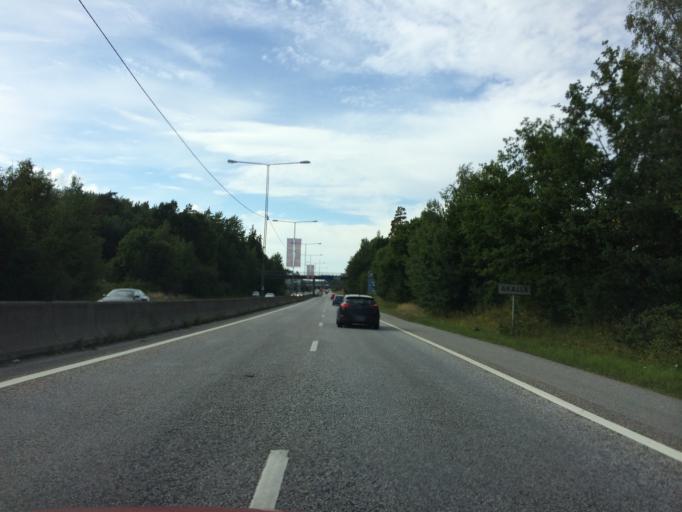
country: SE
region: Stockholm
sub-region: Stockholms Kommun
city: Kista
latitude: 59.4150
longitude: 17.9291
